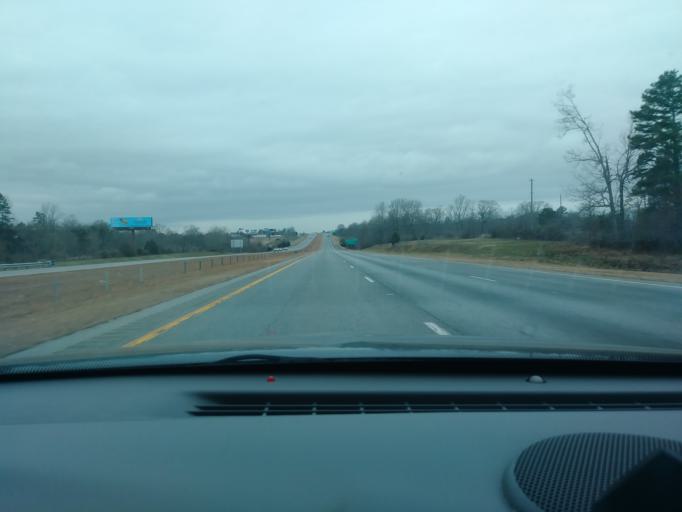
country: US
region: North Carolina
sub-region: Yadkin County
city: Yadkinville
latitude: 36.1171
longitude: -80.7776
